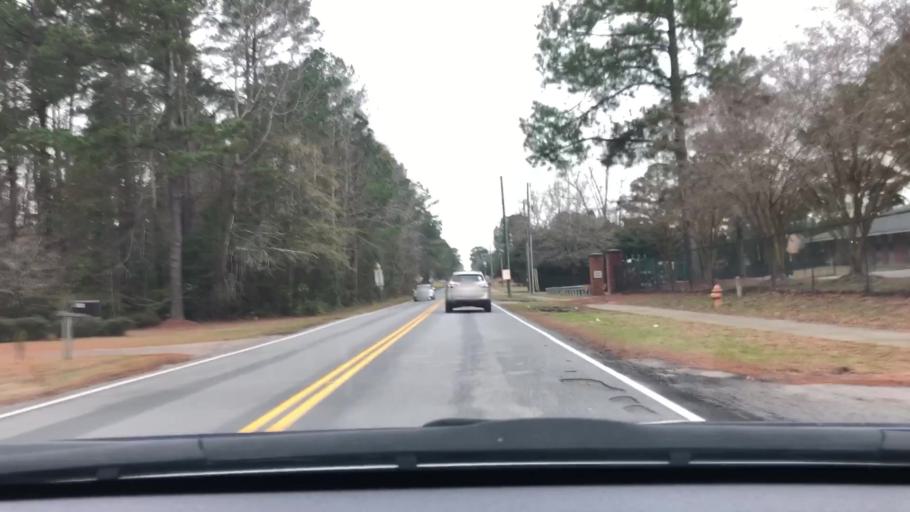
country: US
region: South Carolina
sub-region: Sumter County
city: Cane Savannah
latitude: 33.9349
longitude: -80.4064
